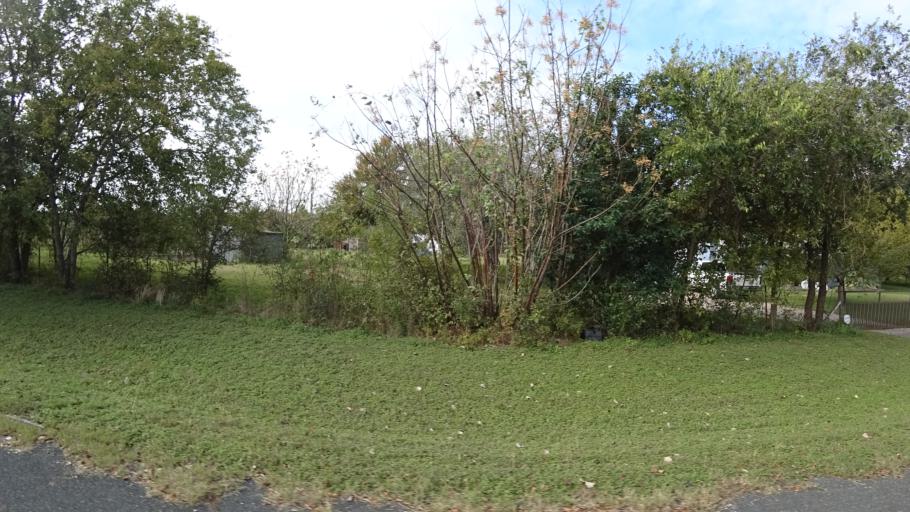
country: US
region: Texas
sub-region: Travis County
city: Manchaca
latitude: 30.1355
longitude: -97.8409
